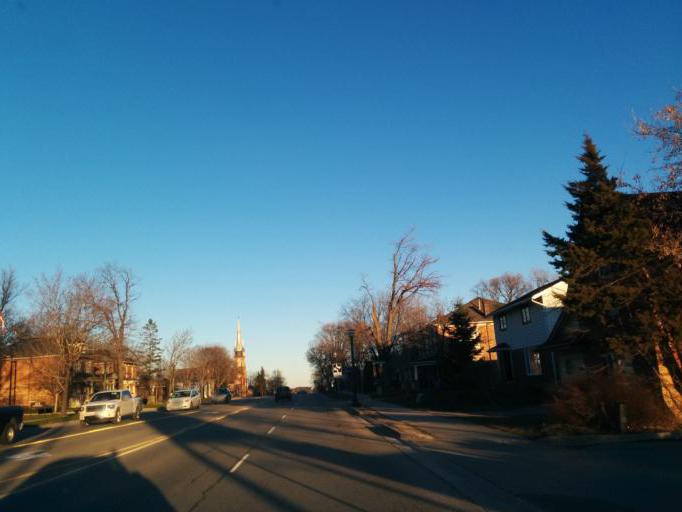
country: CA
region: Ontario
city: Orangeville
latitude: 43.9178
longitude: -80.1037
